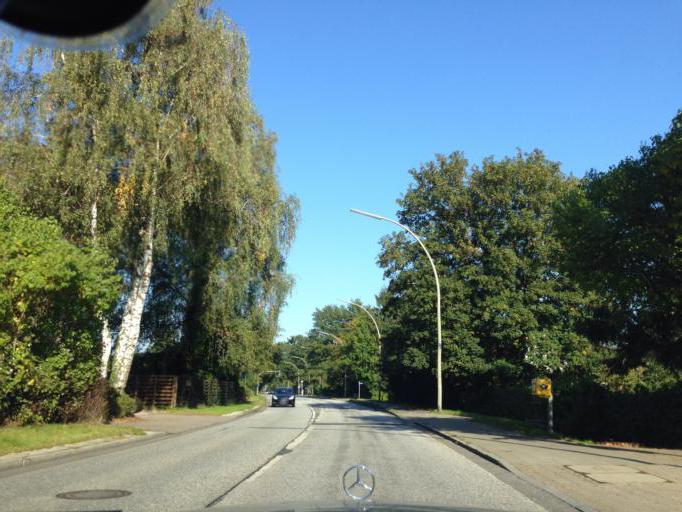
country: DE
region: Schleswig-Holstein
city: Stapelfeld
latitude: 53.6299
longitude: 10.1808
